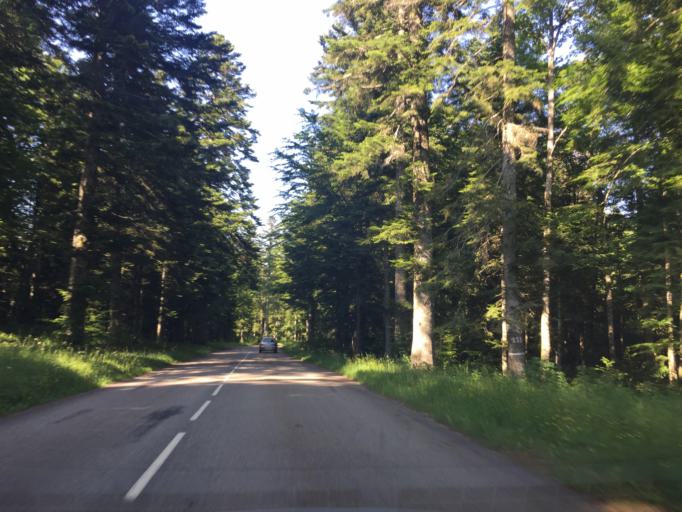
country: FR
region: Rhone-Alpes
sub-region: Departement de la Drome
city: Saint-Jean-en-Royans
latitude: 44.9373
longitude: 5.3071
